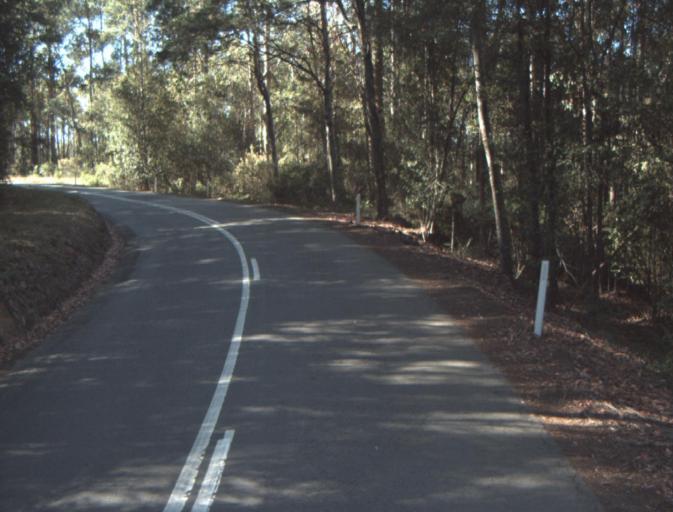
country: AU
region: Tasmania
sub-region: Dorset
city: Scottsdale
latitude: -41.2677
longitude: 147.3821
